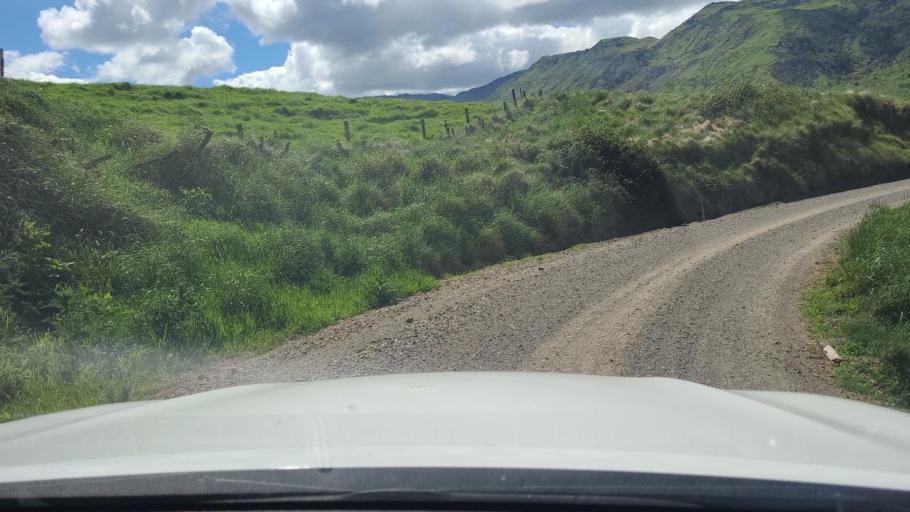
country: NZ
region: Hawke's Bay
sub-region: Napier City
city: Napier
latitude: -39.1625
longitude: 176.6703
